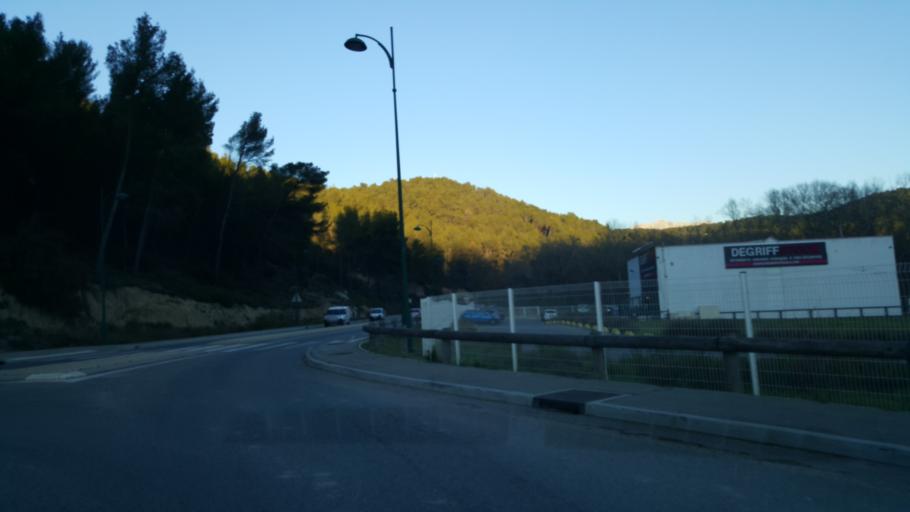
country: FR
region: Provence-Alpes-Cote d'Azur
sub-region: Departement des Bouches-du-Rhone
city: Le Tholonet
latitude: 43.5087
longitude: 5.5012
